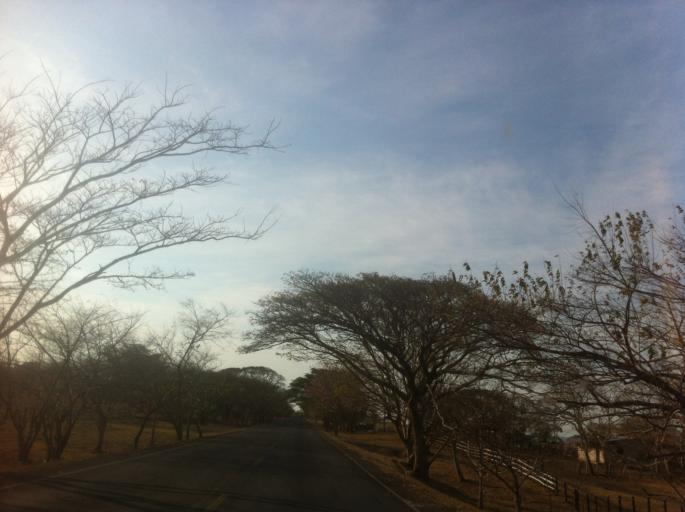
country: NI
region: Rivas
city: Cardenas
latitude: 11.2670
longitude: -85.6473
